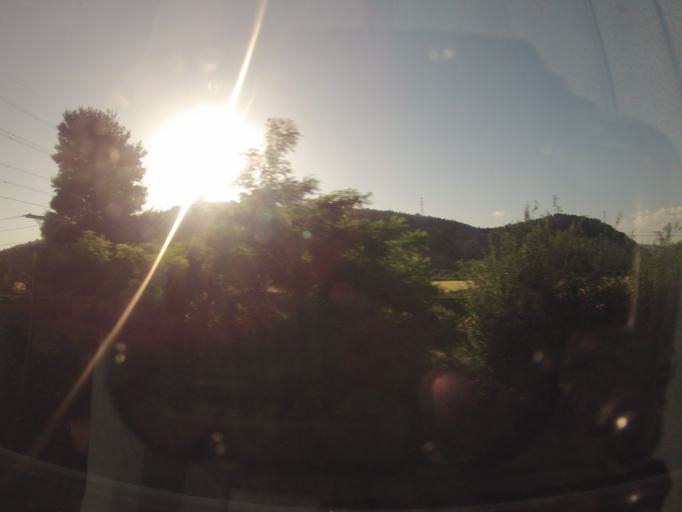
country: CL
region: O'Higgins
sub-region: Provincia de Colchagua
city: Chimbarongo
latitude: -34.6266
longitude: -70.9894
